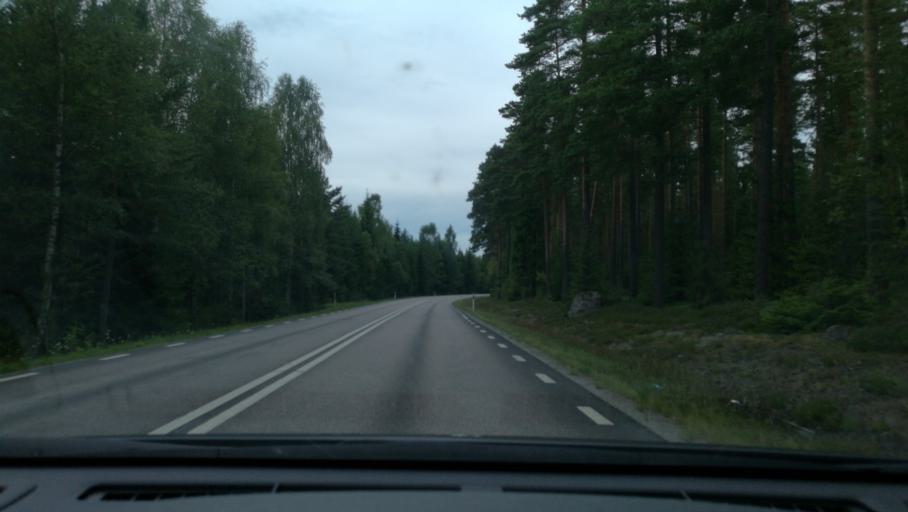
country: SE
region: Soedermanland
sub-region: Katrineholms Kommun
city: Katrineholm
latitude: 59.1230
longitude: 16.1552
